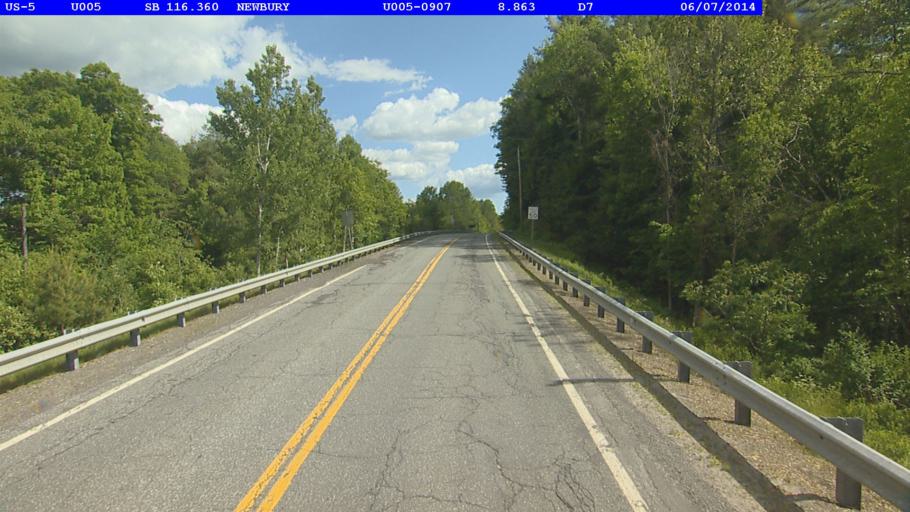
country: US
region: New Hampshire
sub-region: Grafton County
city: Woodsville
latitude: 44.1456
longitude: -72.0430
